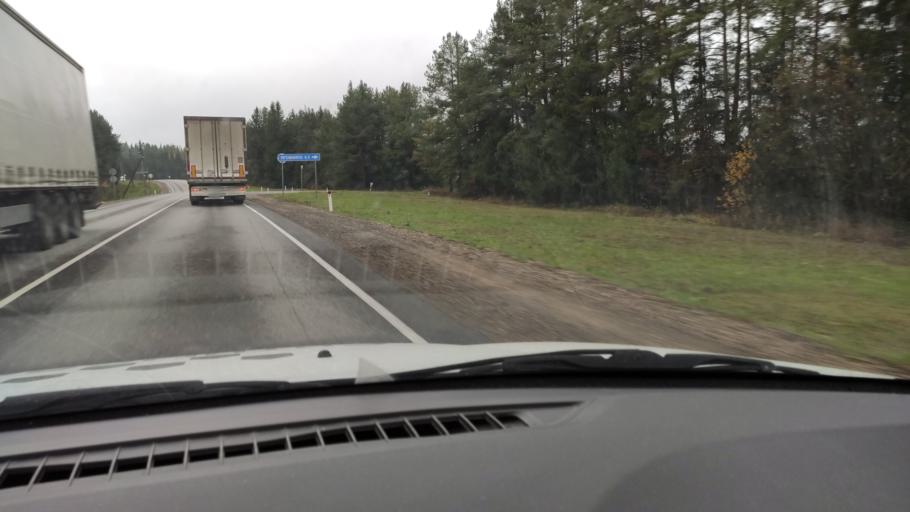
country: RU
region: Kirov
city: Slobodskoy
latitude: 58.7543
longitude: 50.3239
